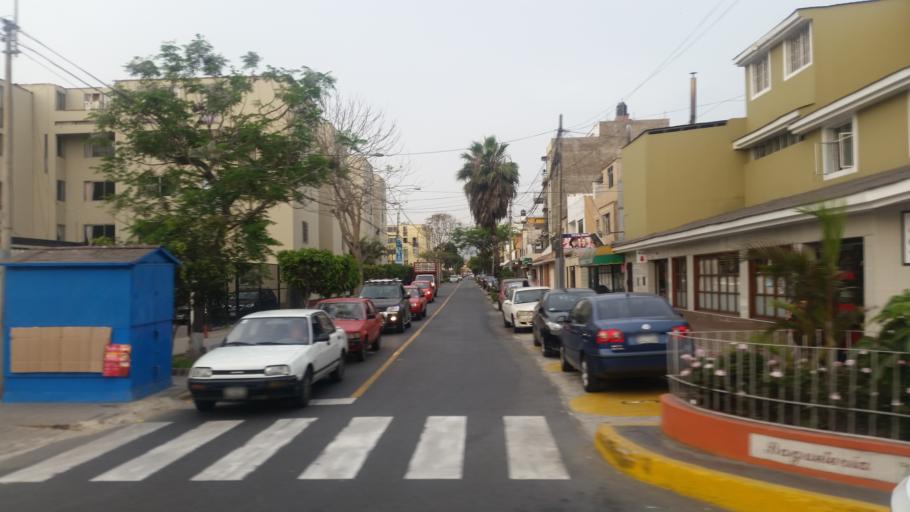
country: PE
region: Lima
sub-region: Lima
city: San Isidro
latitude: -12.0889
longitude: -77.0798
